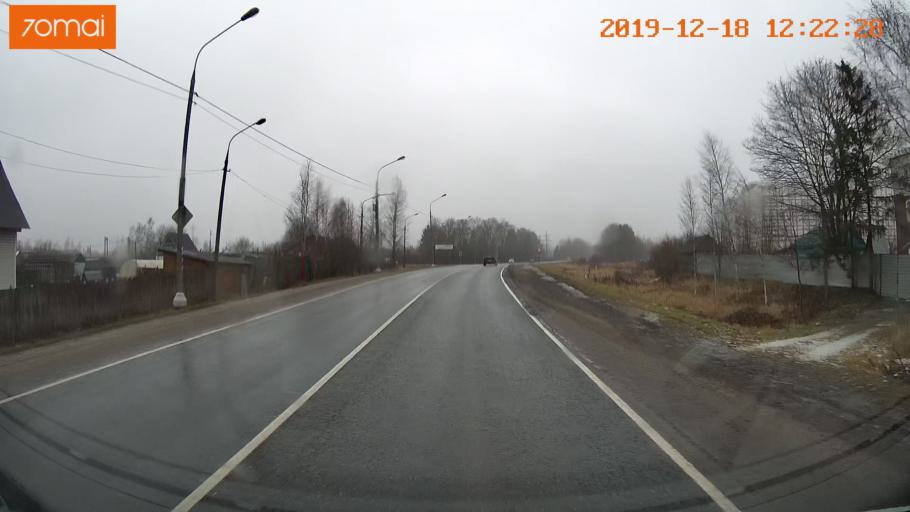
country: RU
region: Moskovskaya
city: Novopetrovskoye
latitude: 56.0061
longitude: 36.4808
